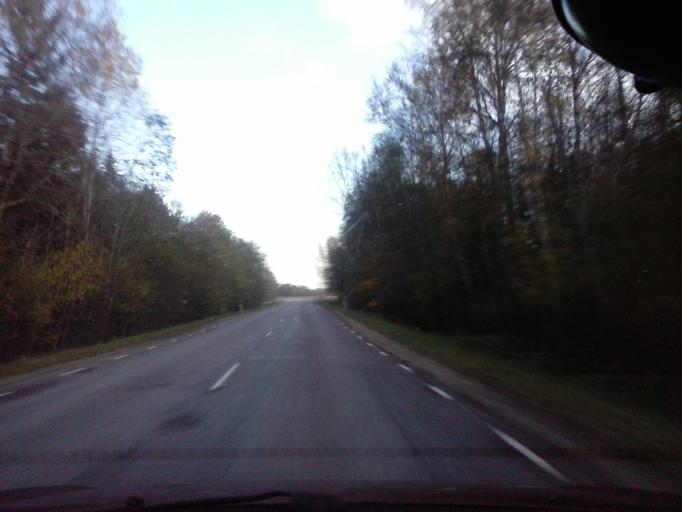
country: EE
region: Harju
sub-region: Nissi vald
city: Turba
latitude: 58.9073
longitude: 24.2091
